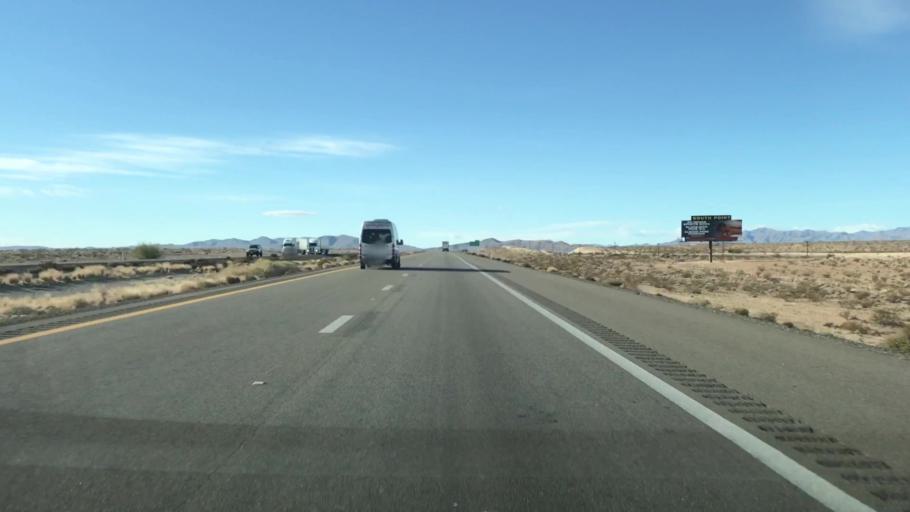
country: US
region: Nevada
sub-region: Clark County
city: Moapa Town
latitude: 36.5121
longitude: -114.7472
